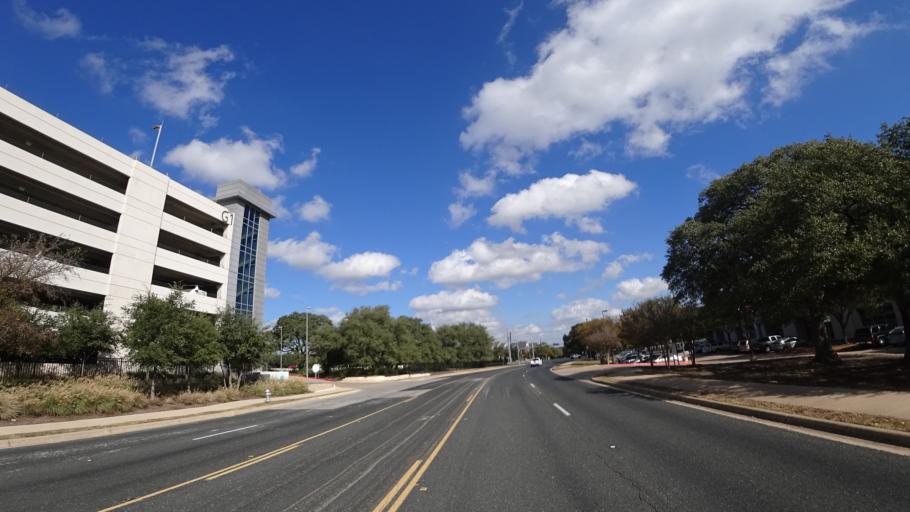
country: US
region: Texas
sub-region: Williamson County
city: Jollyville
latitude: 30.4331
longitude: -97.7327
